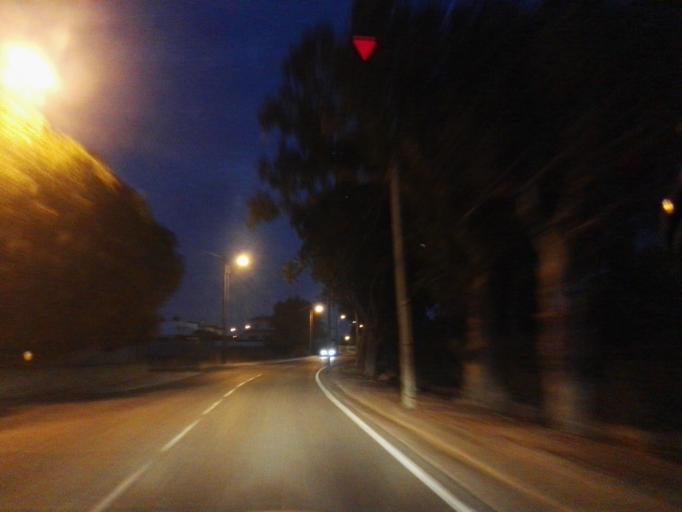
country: PT
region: Lisbon
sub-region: Cascais
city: Cascais
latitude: 38.7173
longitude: -9.4570
